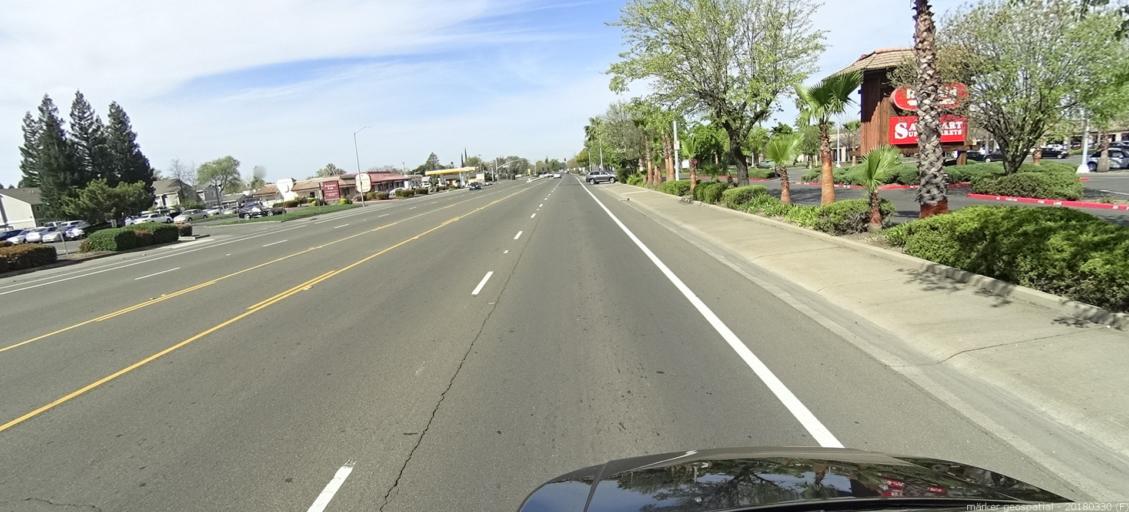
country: US
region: California
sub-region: Sacramento County
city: Rosemont
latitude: 38.5473
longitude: -121.3600
